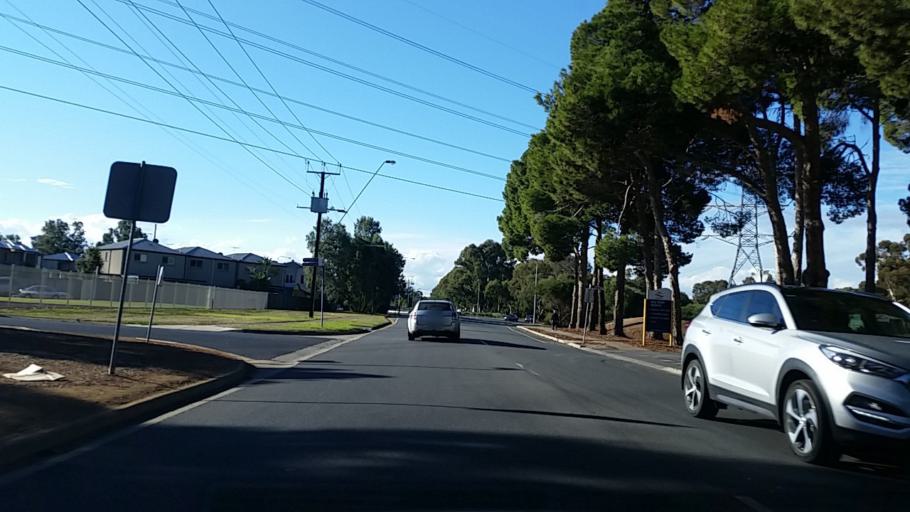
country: AU
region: South Australia
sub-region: Salisbury
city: Salisbury
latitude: -34.7742
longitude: 138.6150
